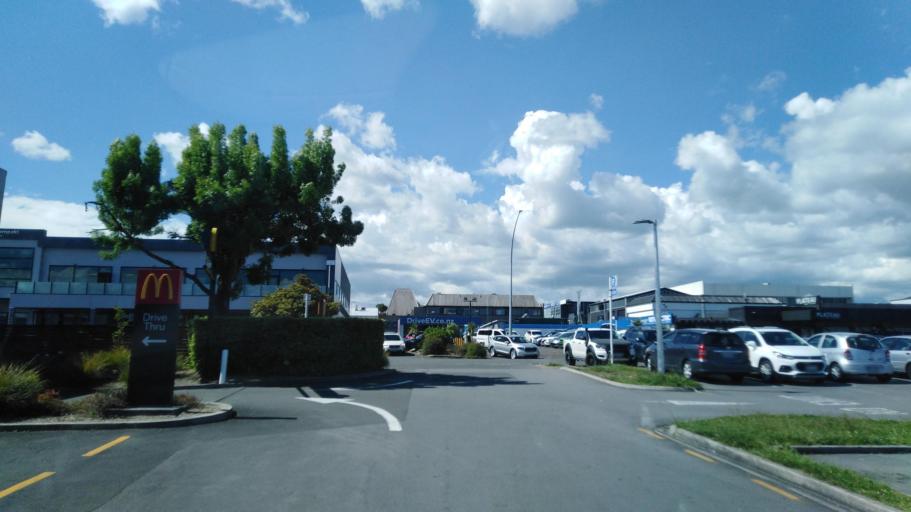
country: NZ
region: Waikato
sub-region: Taupo District
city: Taupo
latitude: -38.6896
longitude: 176.0722
